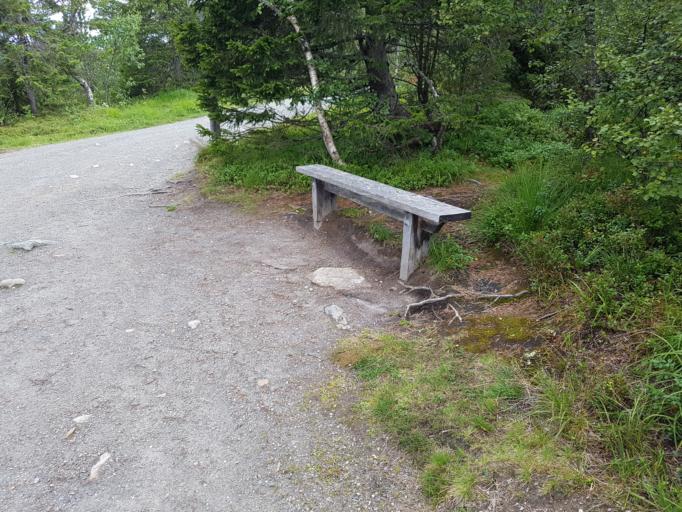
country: NO
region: Sor-Trondelag
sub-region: Melhus
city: Melhus
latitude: 63.4151
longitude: 10.2449
